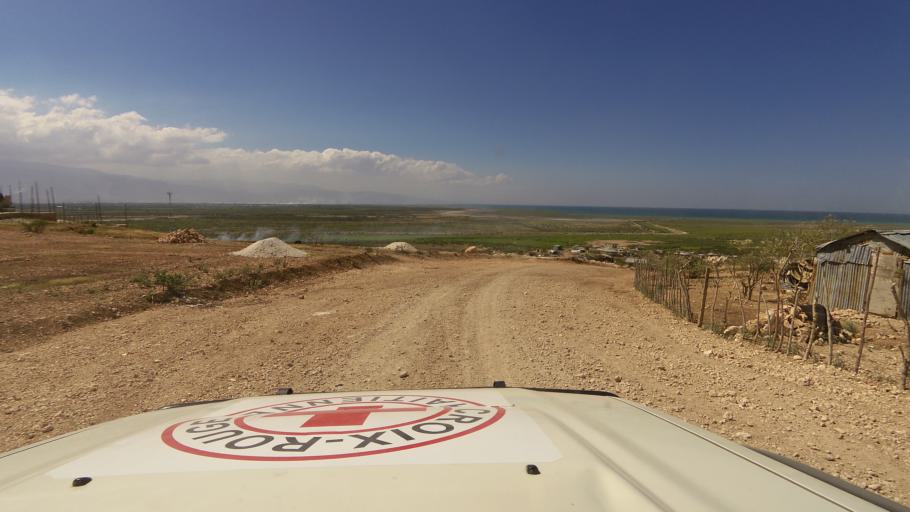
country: HT
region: Ouest
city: Croix des Bouquets
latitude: 18.6667
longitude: -72.2934
